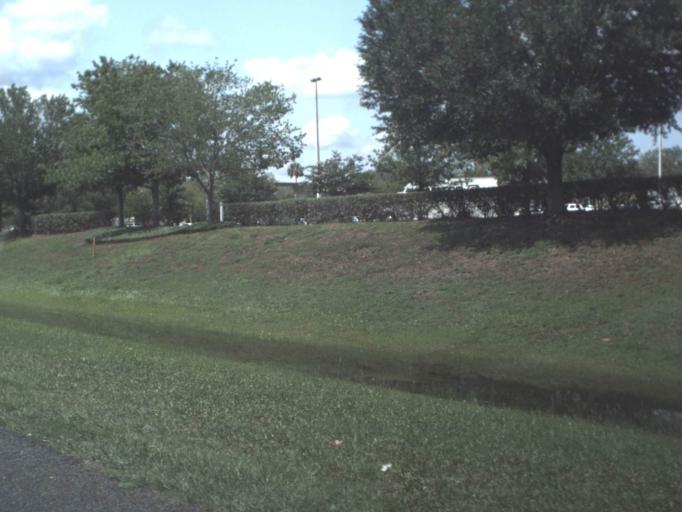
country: US
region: Florida
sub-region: Saint Johns County
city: Fruit Cove
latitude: 30.1869
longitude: -81.5518
